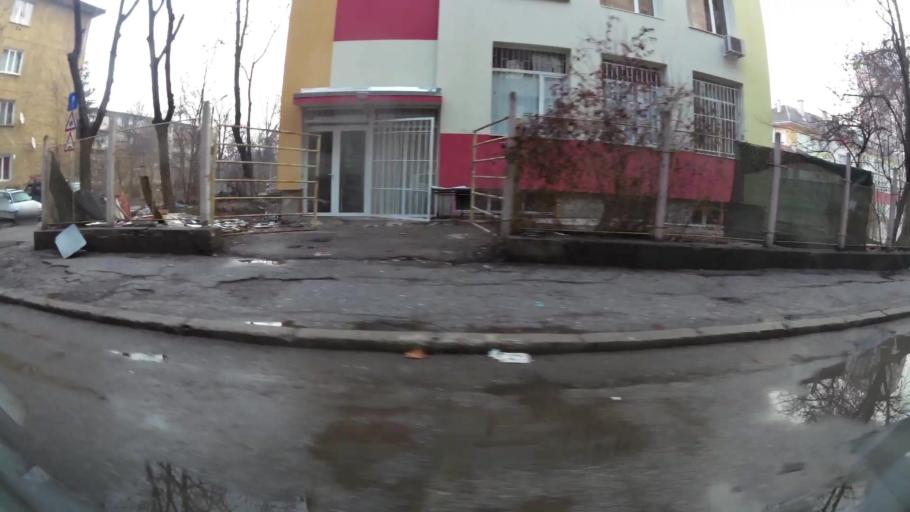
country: BG
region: Sofia-Capital
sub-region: Stolichna Obshtina
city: Sofia
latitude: 42.7285
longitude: 23.3111
